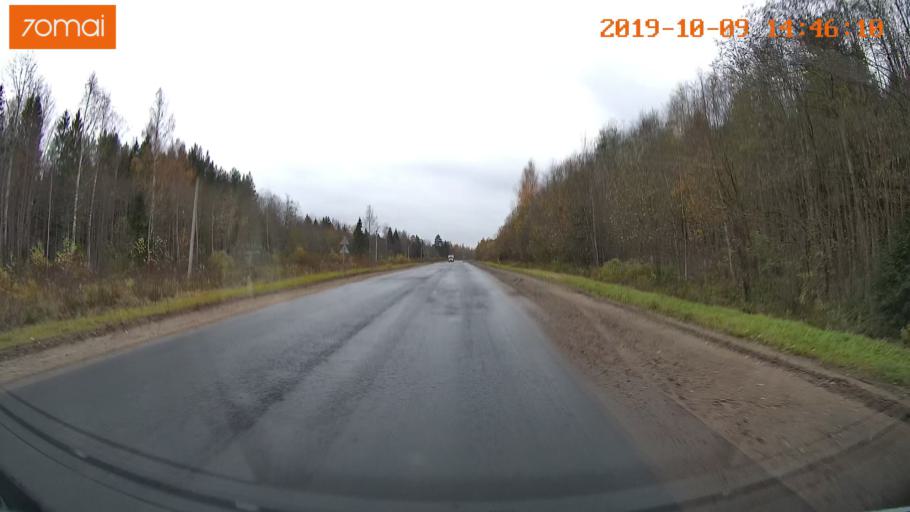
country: RU
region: Kostroma
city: Buy
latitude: 58.4348
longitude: 41.5771
